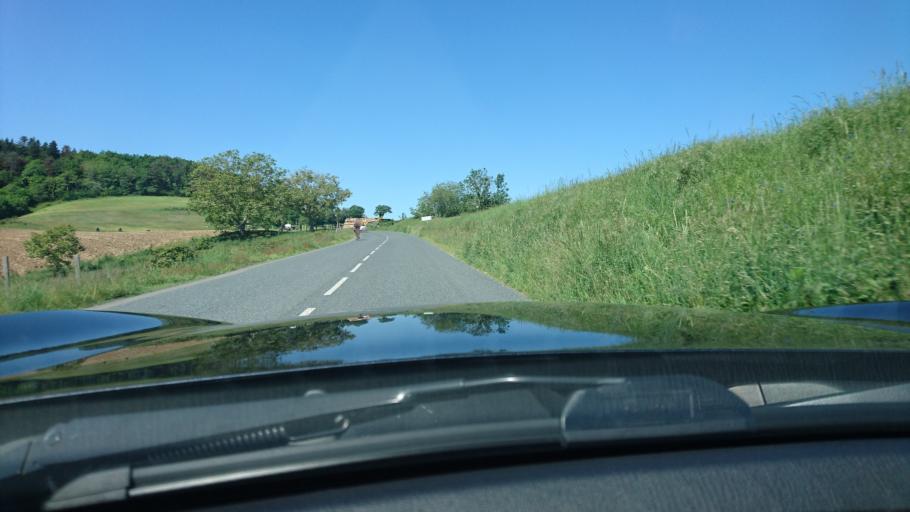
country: FR
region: Rhone-Alpes
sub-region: Departement du Rhone
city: Montrottier
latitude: 45.7990
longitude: 4.4535
